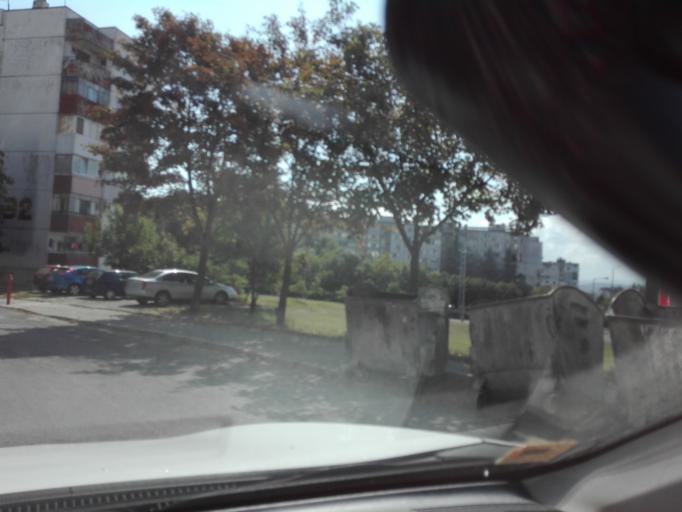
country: BG
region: Burgas
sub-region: Obshtina Burgas
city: Burgas
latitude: 42.4584
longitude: 27.4172
